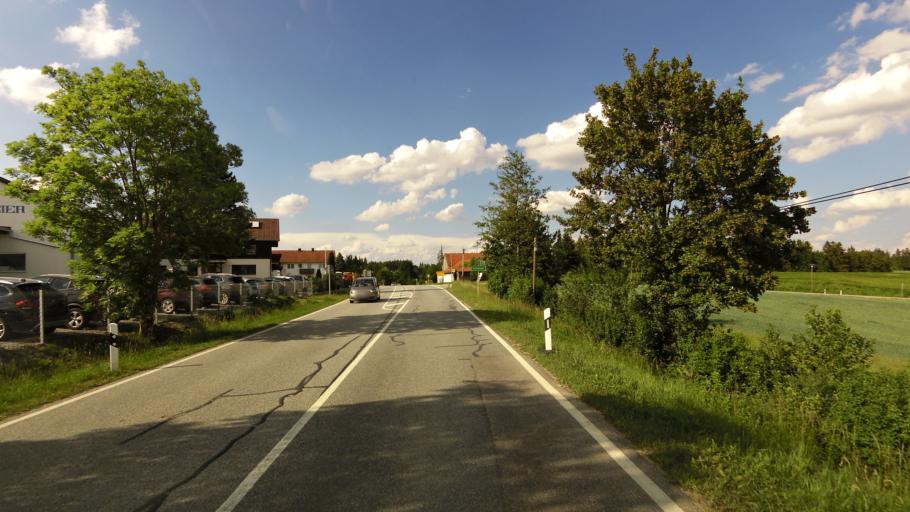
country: DE
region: Bavaria
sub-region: Lower Bavaria
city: Vilsheim
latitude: 48.4287
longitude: 12.1386
